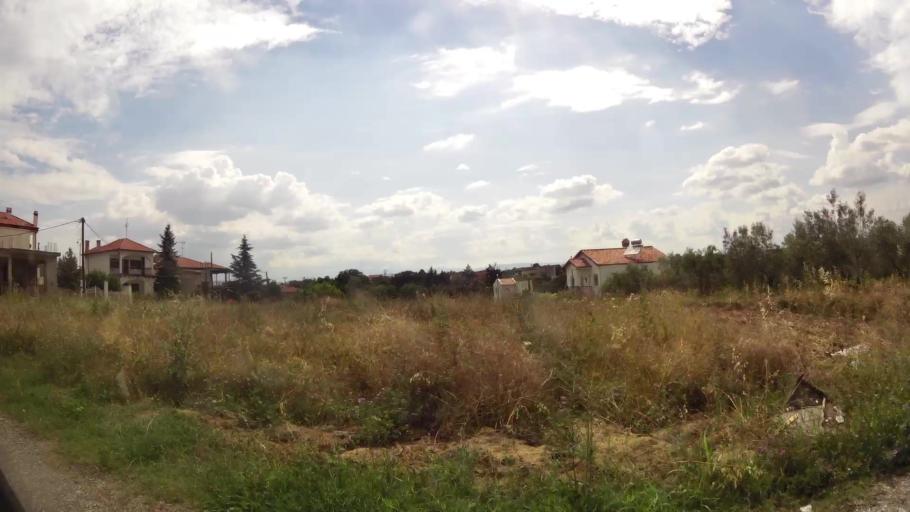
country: GR
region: Central Macedonia
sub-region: Nomos Pierias
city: Makrygialos
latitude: 40.4195
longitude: 22.6073
